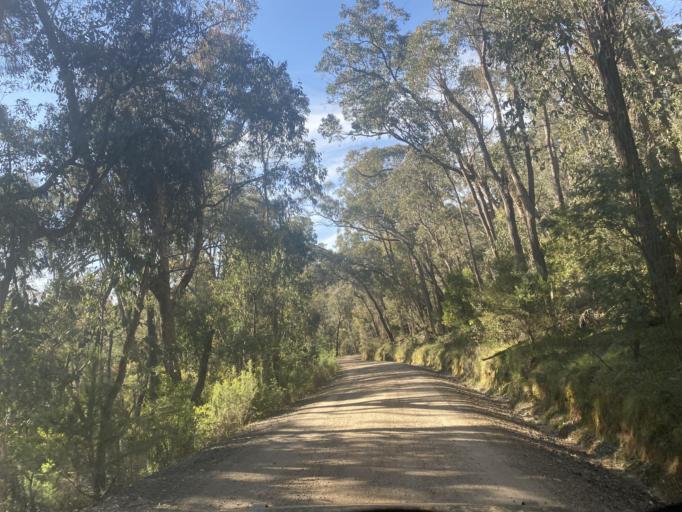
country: AU
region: Victoria
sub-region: Mansfield
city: Mansfield
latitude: -36.8295
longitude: 146.1588
